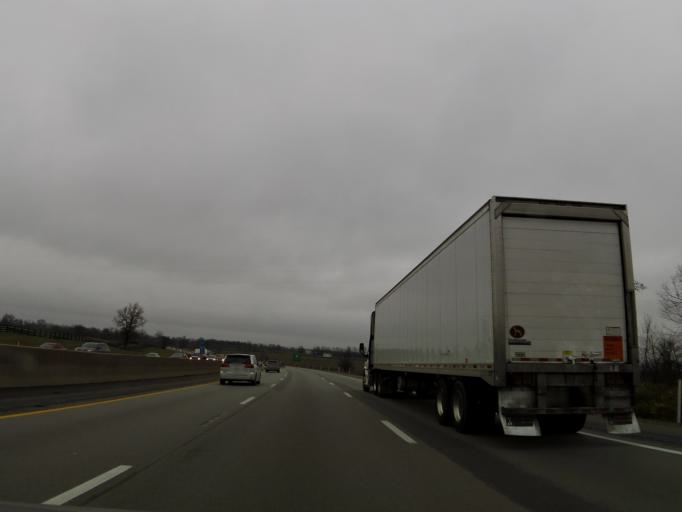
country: US
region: Kentucky
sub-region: Scott County
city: Georgetown
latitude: 38.1699
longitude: -84.5366
